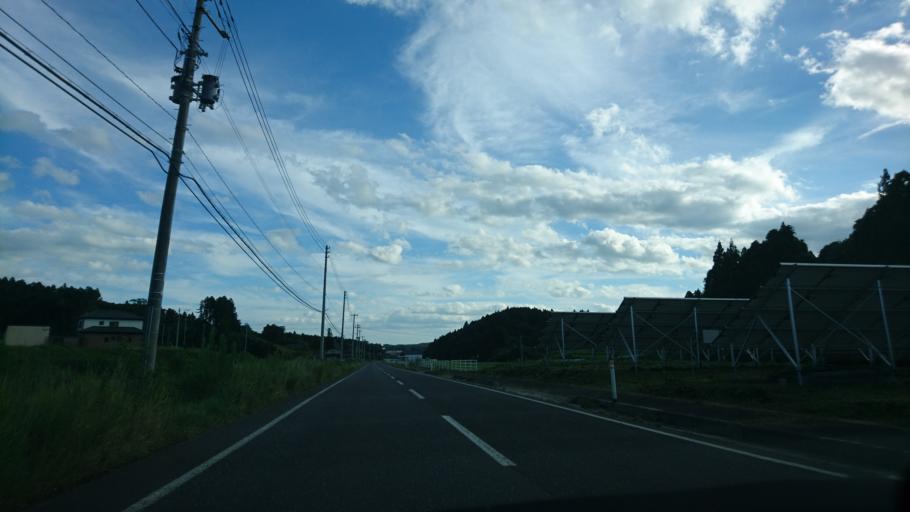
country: JP
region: Iwate
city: Ichinoseki
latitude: 38.8594
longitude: 141.1846
